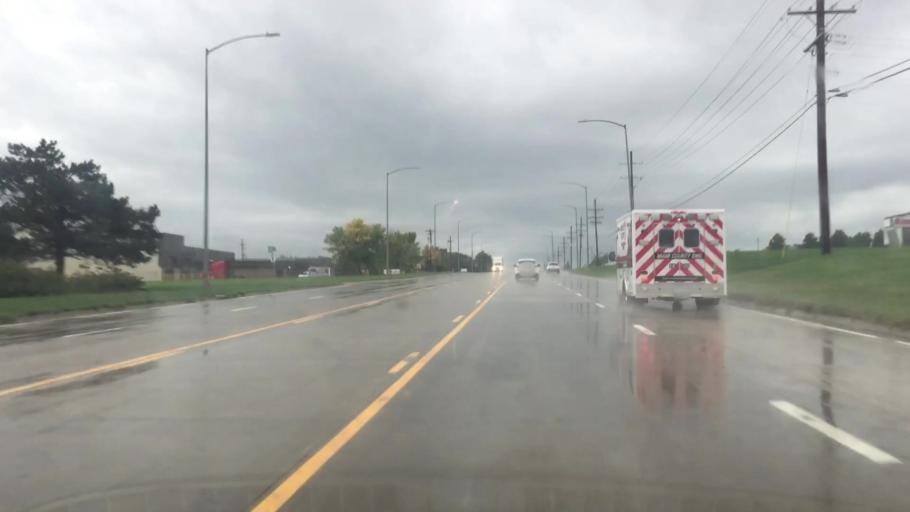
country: US
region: Kansas
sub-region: Johnson County
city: Olathe
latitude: 38.8458
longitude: -94.8160
